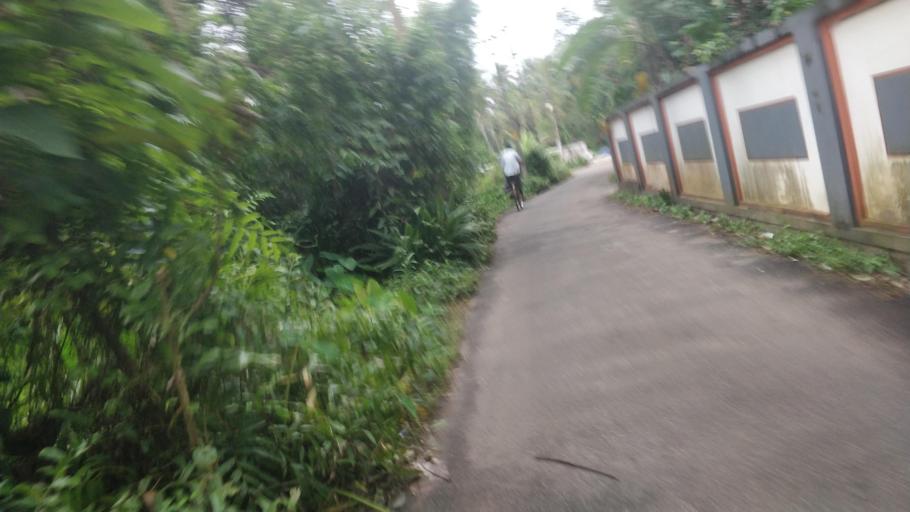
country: IN
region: Kerala
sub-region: Alappuzha
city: Shertallai
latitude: 9.6873
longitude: 76.3477
